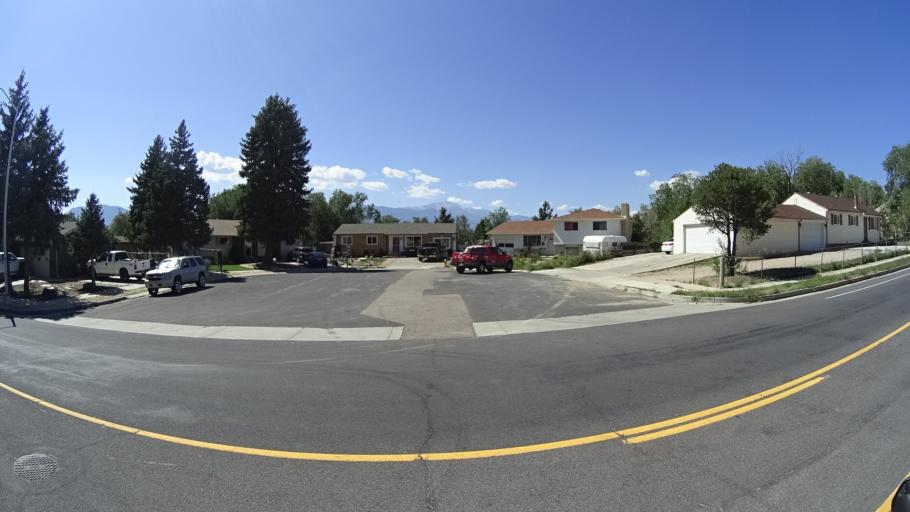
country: US
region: Colorado
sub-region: El Paso County
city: Cimarron Hills
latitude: 38.8280
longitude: -104.7487
